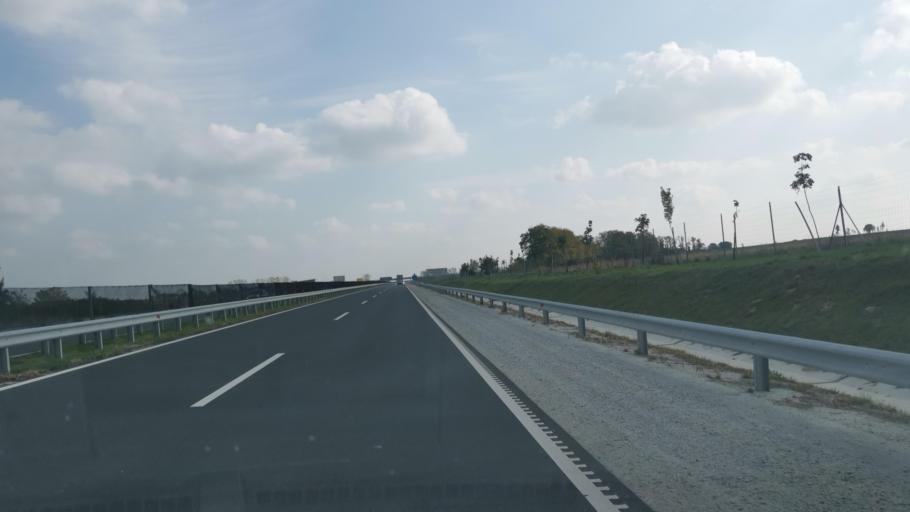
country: HU
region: Gyor-Moson-Sopron
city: Nagycenk
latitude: 47.5962
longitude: 16.6983
